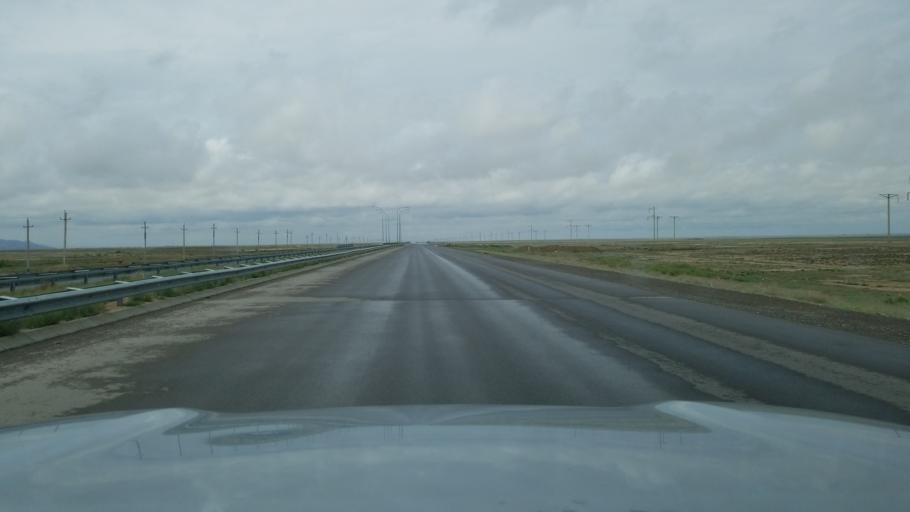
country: TM
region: Balkan
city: Gazanjyk
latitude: 39.1927
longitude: 55.7828
